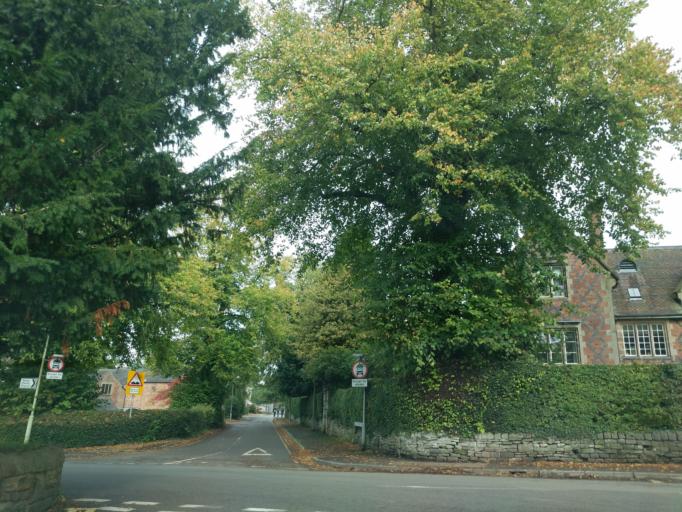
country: GB
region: England
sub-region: Staffordshire
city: Audley
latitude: 53.0037
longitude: -2.2870
